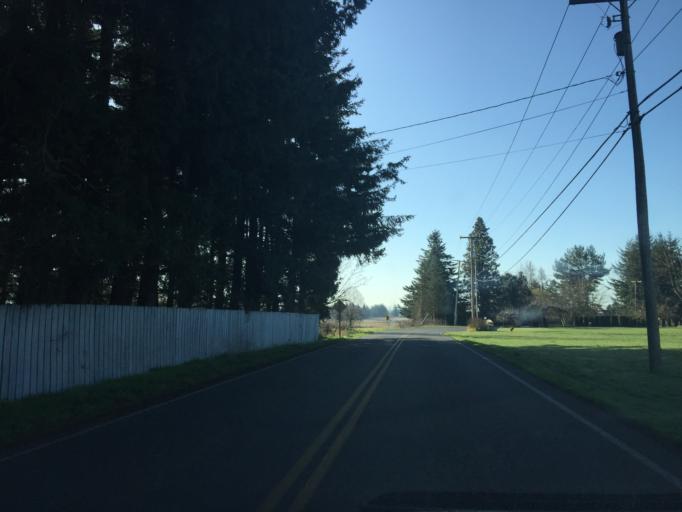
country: US
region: Washington
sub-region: Whatcom County
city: Lynden
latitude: 48.9090
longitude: -122.4644
